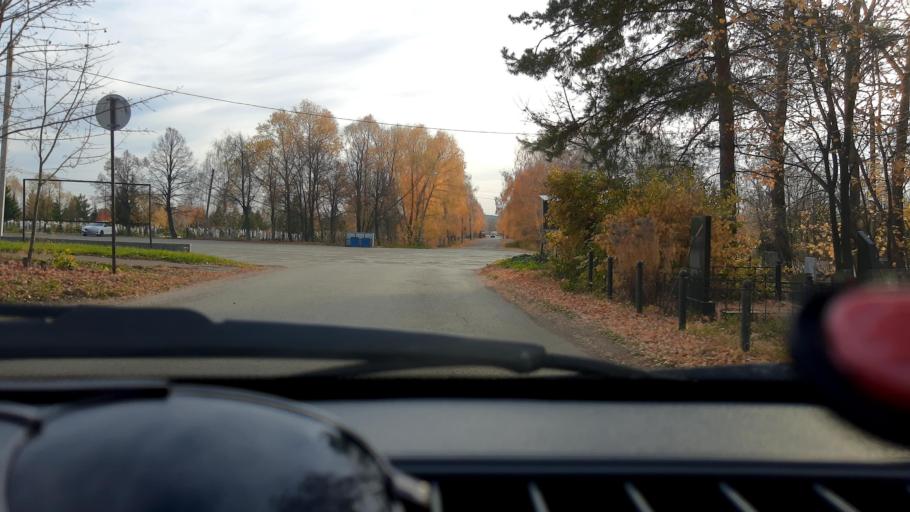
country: RU
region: Bashkortostan
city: Ufa
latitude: 54.8515
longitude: 56.1552
